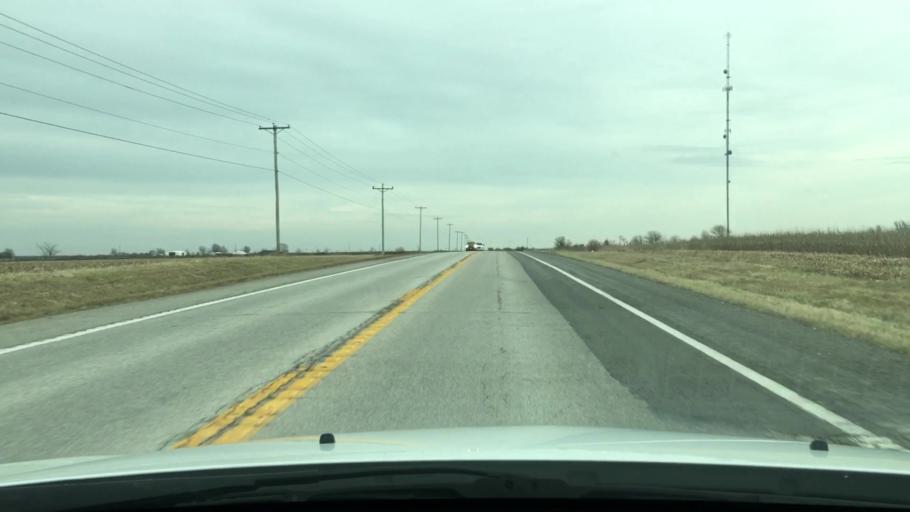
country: US
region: Missouri
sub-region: Pike County
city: Bowling Green
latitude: 39.3448
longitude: -91.3115
